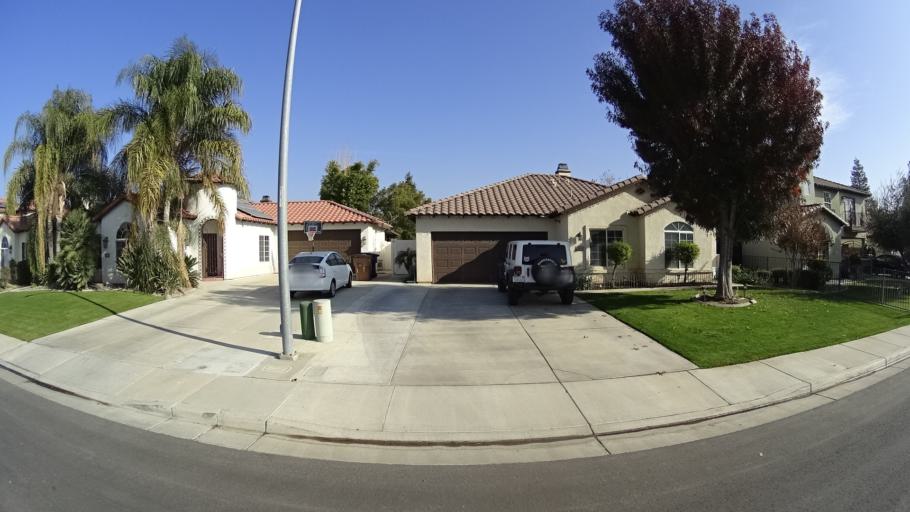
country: US
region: California
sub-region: Kern County
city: Rosedale
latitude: 35.3572
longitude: -119.1676
